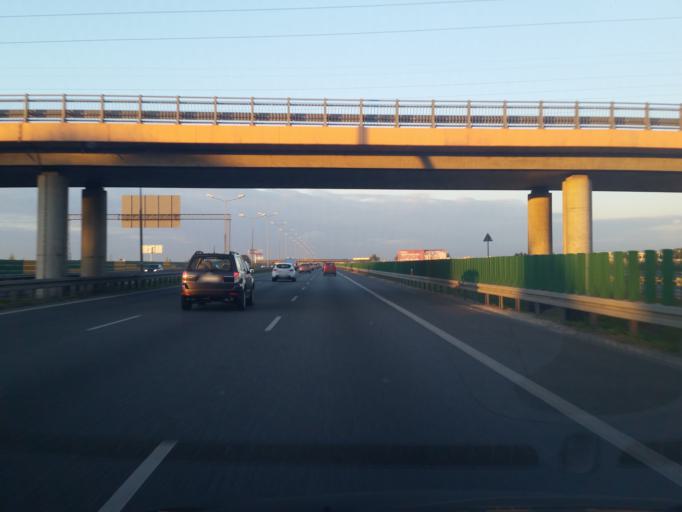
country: PL
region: Masovian Voivodeship
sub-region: Warszawa
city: Ursus
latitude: 52.2229
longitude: 20.8713
